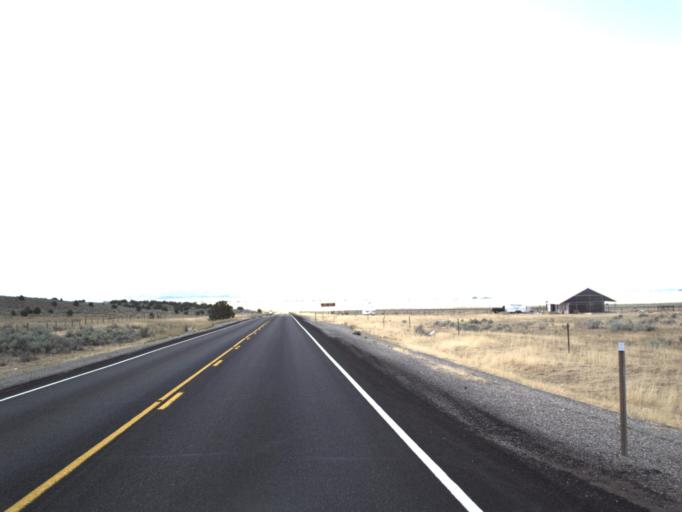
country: US
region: Utah
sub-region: Millard County
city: Fillmore
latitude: 39.1432
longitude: -112.2389
